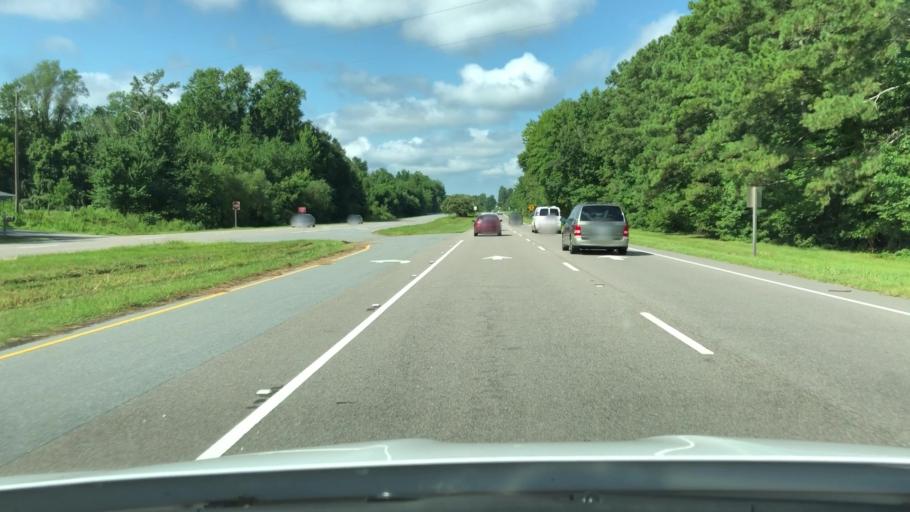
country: US
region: North Carolina
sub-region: Perquimans County
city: Hertford
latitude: 36.1691
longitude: -76.4706
